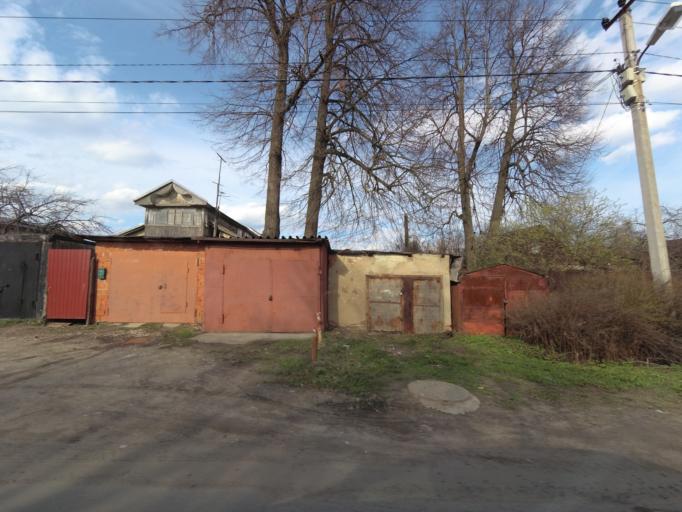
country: RU
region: Moskovskaya
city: Lobnya
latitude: 56.0208
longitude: 37.4361
